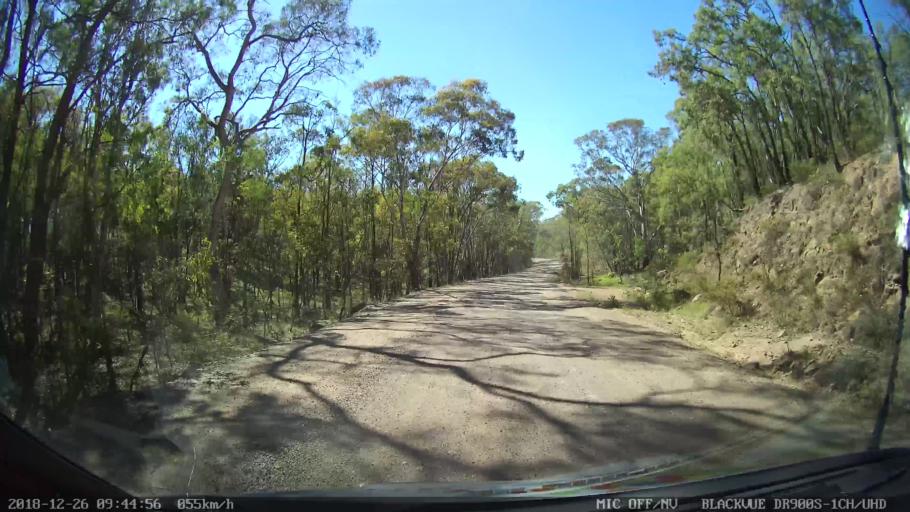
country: AU
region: New South Wales
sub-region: Mid-Western Regional
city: Kandos
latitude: -32.9599
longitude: 150.0997
